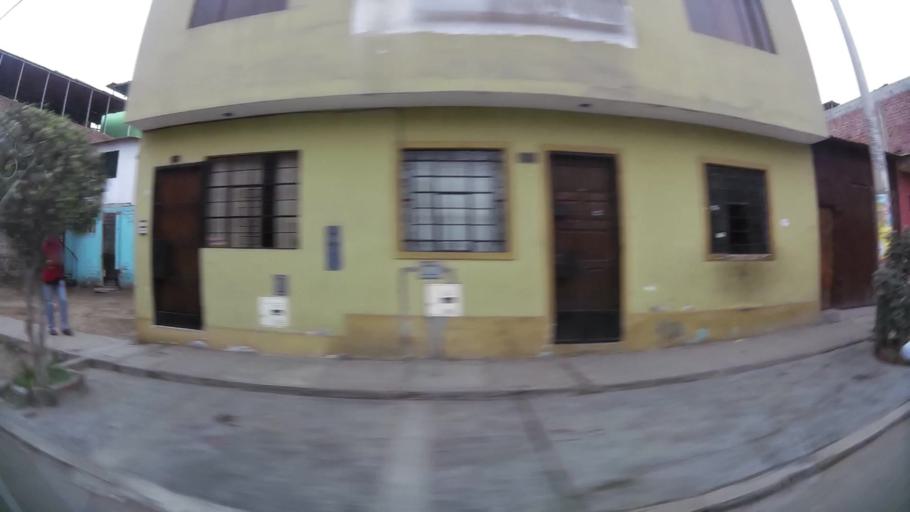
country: PE
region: Lima
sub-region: Lima
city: Surco
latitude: -12.1499
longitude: -76.9722
